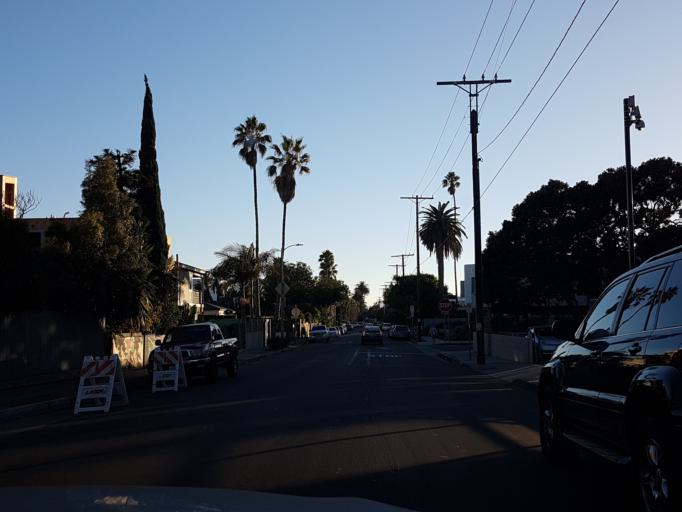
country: US
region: California
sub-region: Los Angeles County
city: Marina del Rey
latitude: 33.9946
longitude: -118.4633
